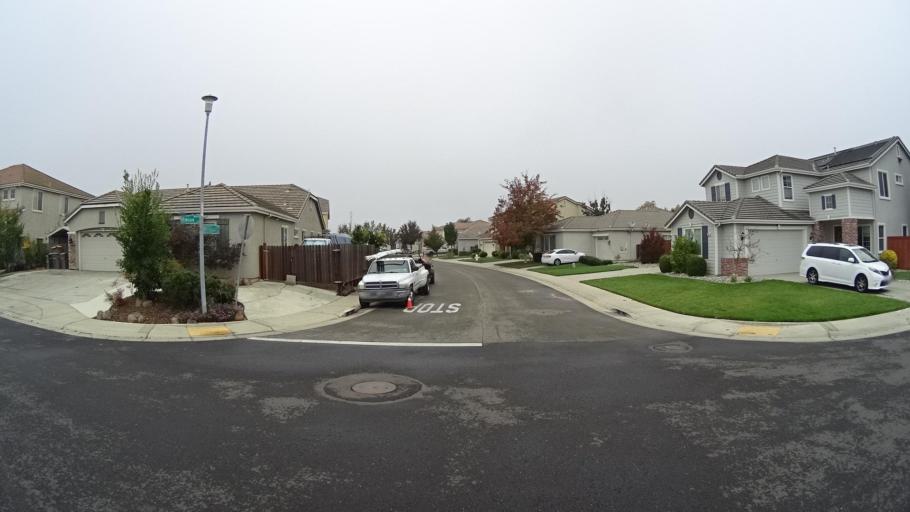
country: US
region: California
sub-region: Sacramento County
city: Elk Grove
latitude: 38.4013
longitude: -121.3440
